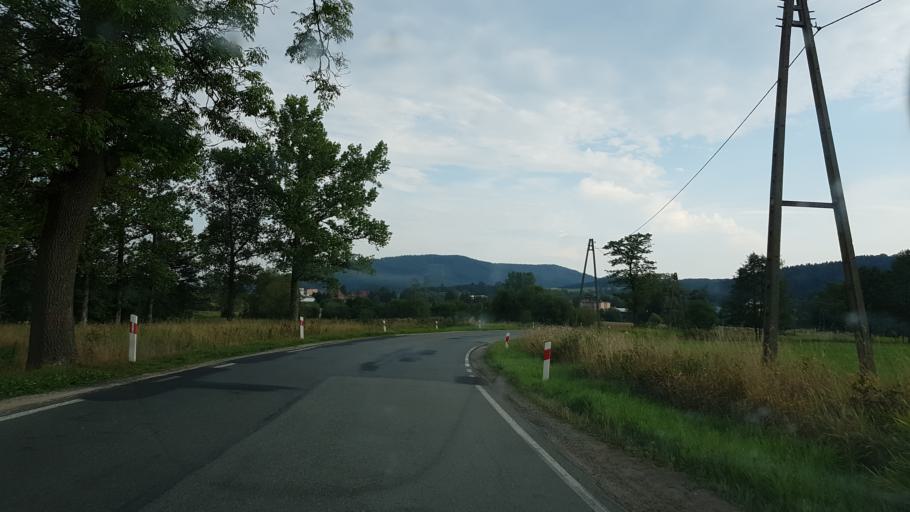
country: PL
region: Lower Silesian Voivodeship
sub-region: Powiat kamiennogorski
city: Marciszow
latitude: 50.8593
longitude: 16.0030
